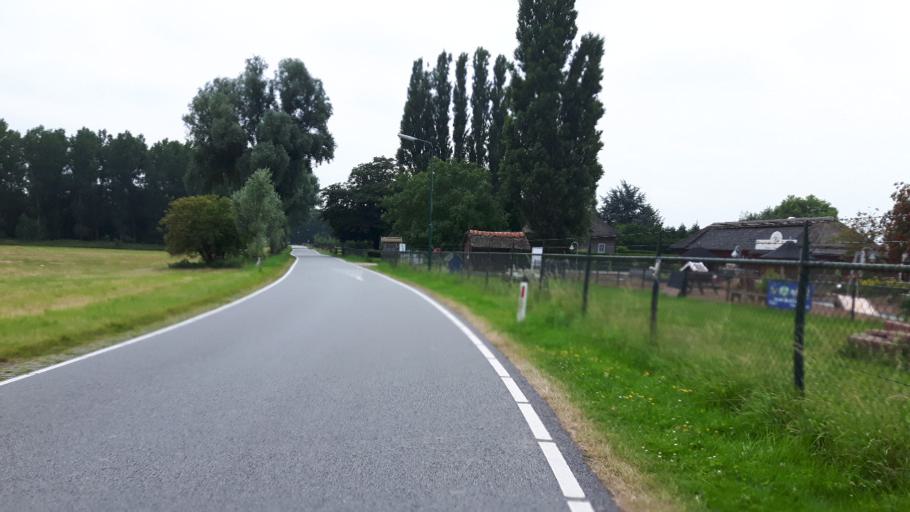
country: NL
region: Utrecht
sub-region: Gemeente IJsselstein
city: IJsselstein
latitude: 52.0397
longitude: 5.0355
